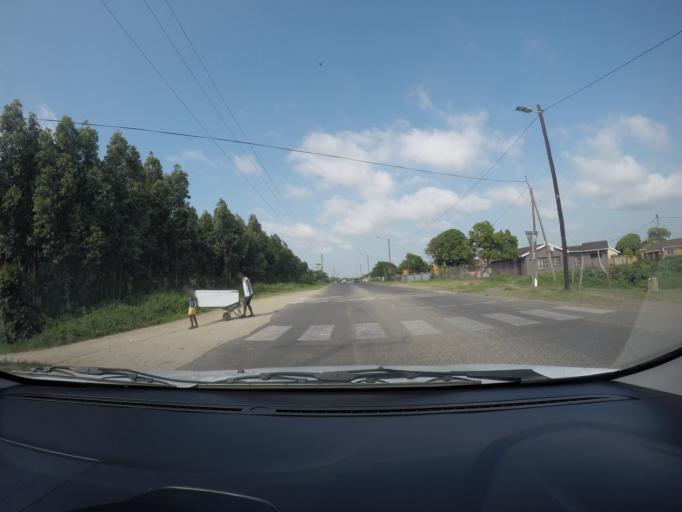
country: ZA
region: KwaZulu-Natal
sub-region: uThungulu District Municipality
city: eSikhawini
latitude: -28.8707
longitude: 31.9253
